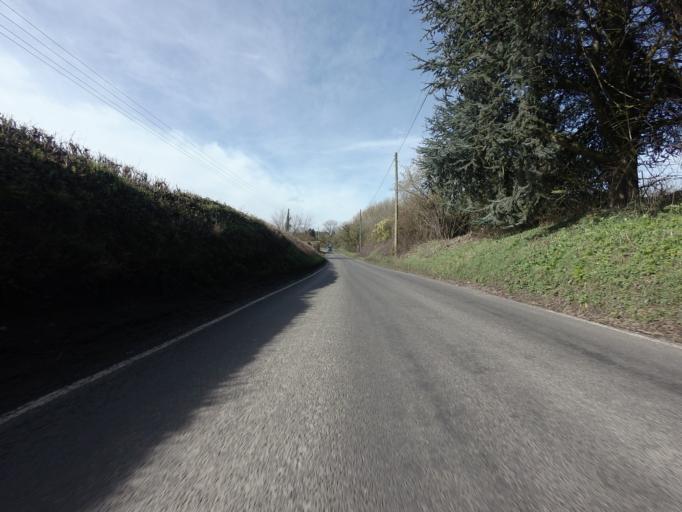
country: GB
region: England
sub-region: Kent
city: Swanley
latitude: 51.3836
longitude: 0.1703
